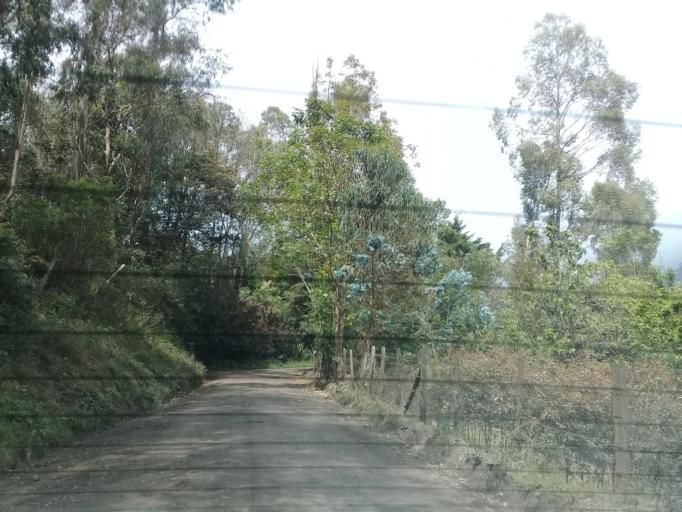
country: CO
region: Cundinamarca
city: Caqueza
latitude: 4.4131
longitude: -73.9844
